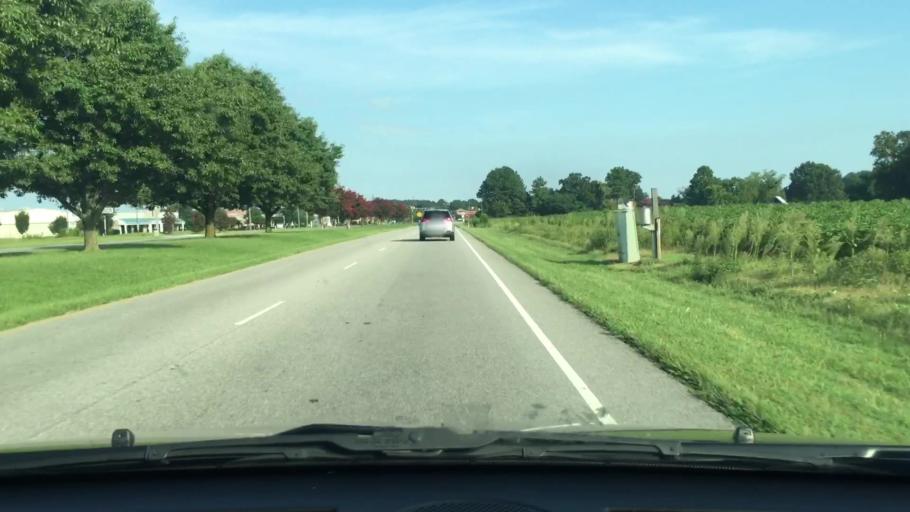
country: US
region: Virginia
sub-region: Isle of Wight County
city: Carrollton
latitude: 36.9517
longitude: -76.5984
